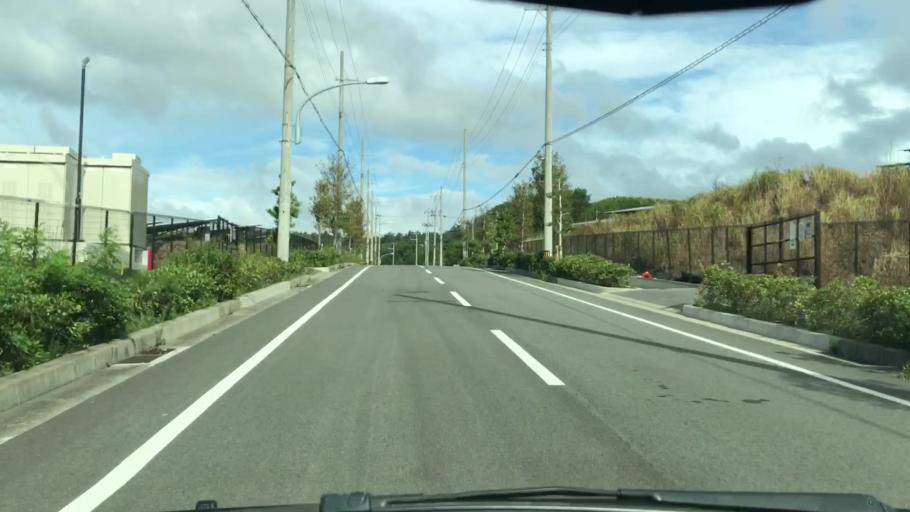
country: JP
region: Hyogo
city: Takarazuka
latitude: 34.8374
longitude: 135.3050
